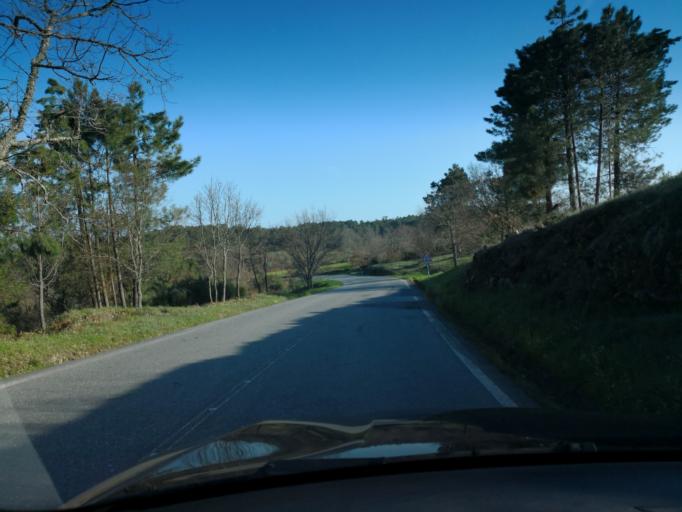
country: PT
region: Vila Real
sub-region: Sabrosa
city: Sabrosa
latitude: 41.3548
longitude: -7.6130
